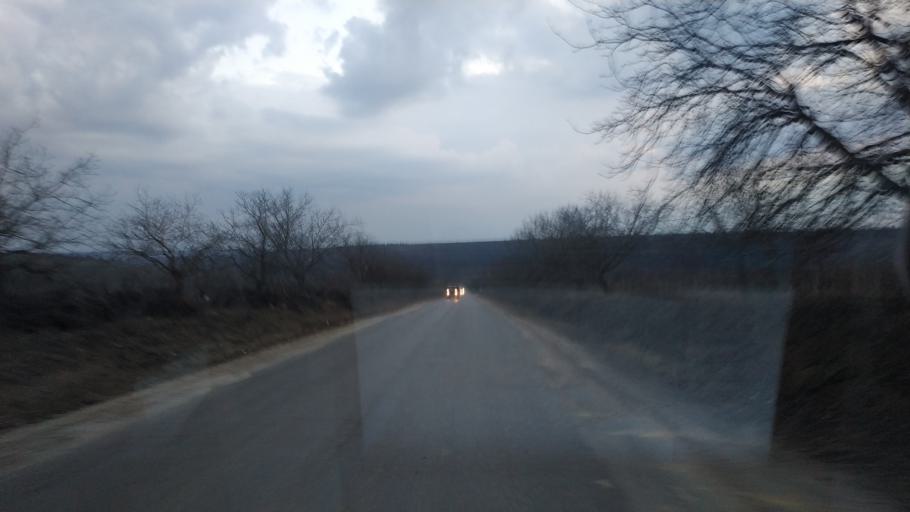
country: MD
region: Anenii Noi
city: Anenii Noi
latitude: 46.9604
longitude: 29.2842
